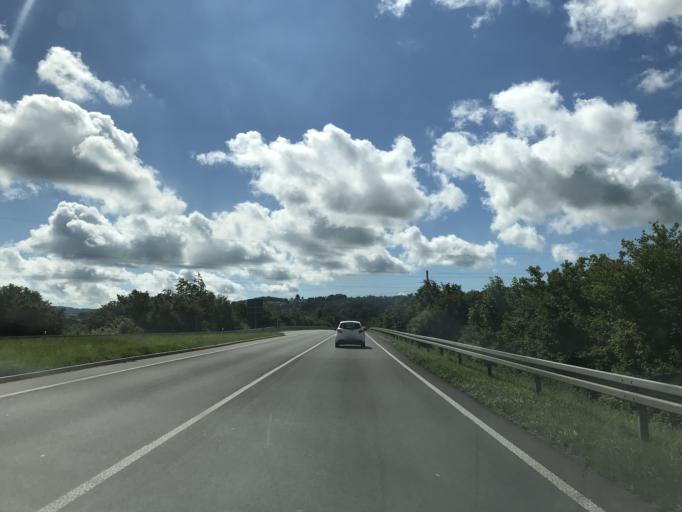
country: DE
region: Baden-Wuerttemberg
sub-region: Freiburg Region
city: Maulburg
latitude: 47.6467
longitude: 7.7935
